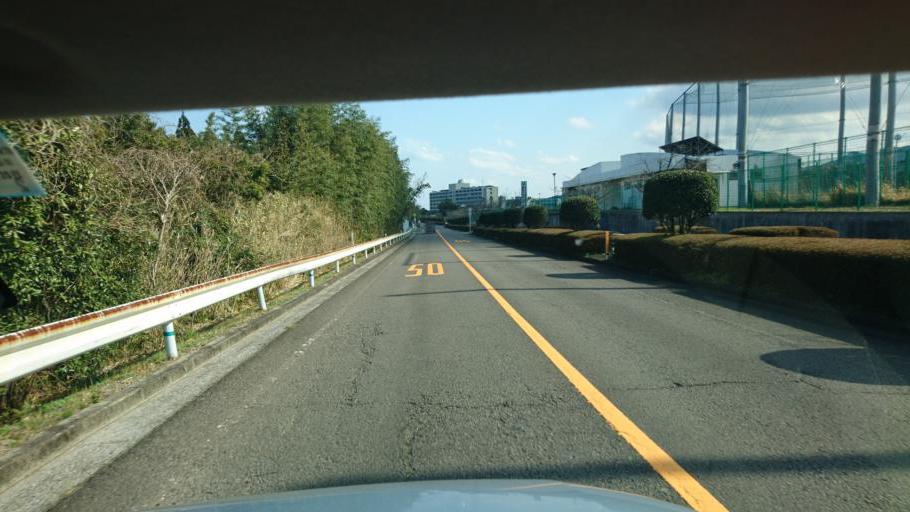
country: JP
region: Miyazaki
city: Miyazaki-shi
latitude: 31.8340
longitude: 131.4087
